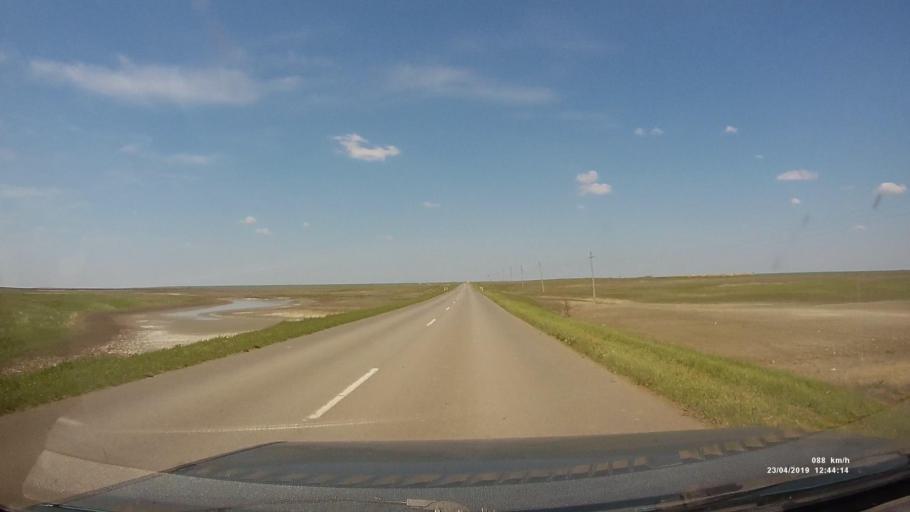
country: RU
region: Kalmykiya
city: Yashalta
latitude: 46.4742
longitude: 42.6485
